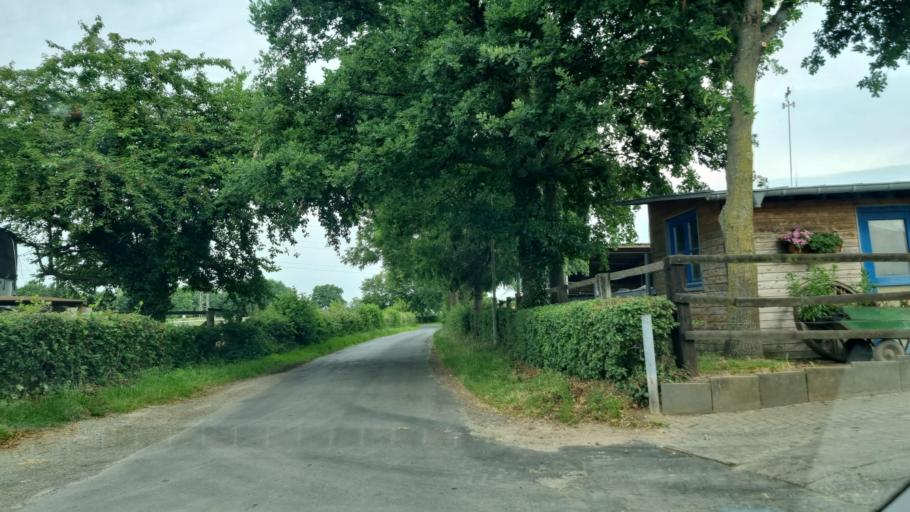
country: DE
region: North Rhine-Westphalia
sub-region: Regierungsbezirk Dusseldorf
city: Voerde
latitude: 51.6016
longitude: 6.6685
